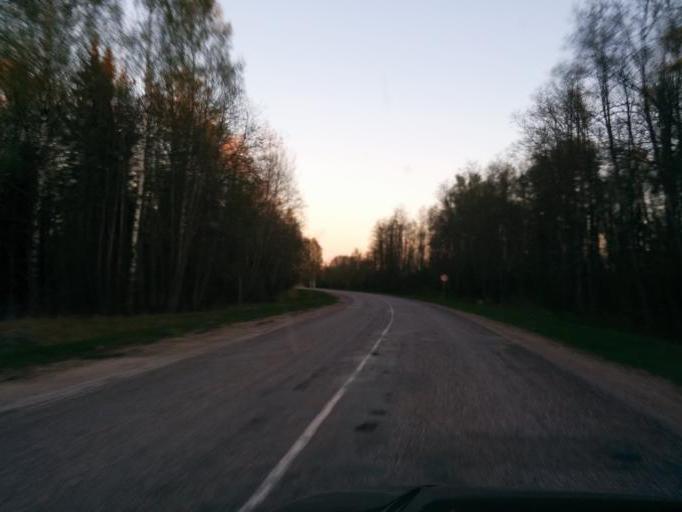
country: LV
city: Tireli
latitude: 56.8380
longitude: 23.5429
